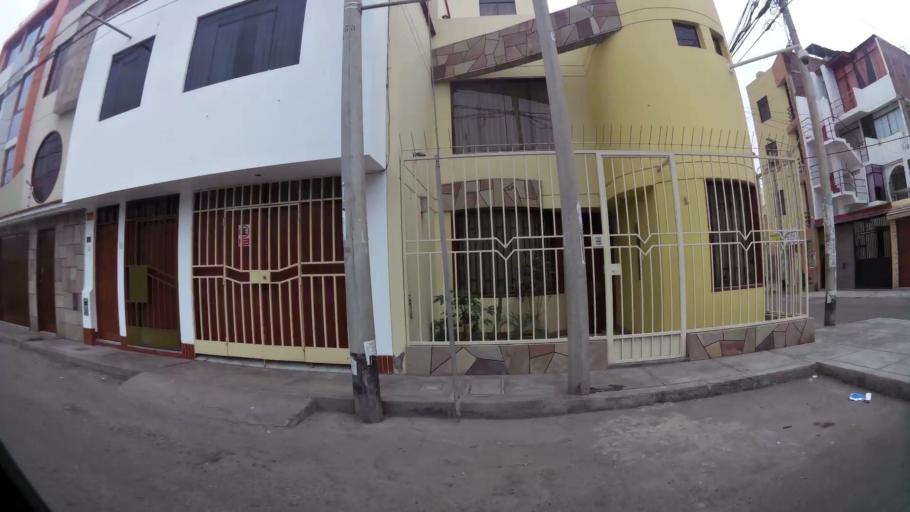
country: PE
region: La Libertad
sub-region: Provincia de Trujillo
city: Buenos Aires
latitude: -8.1324
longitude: -79.0356
